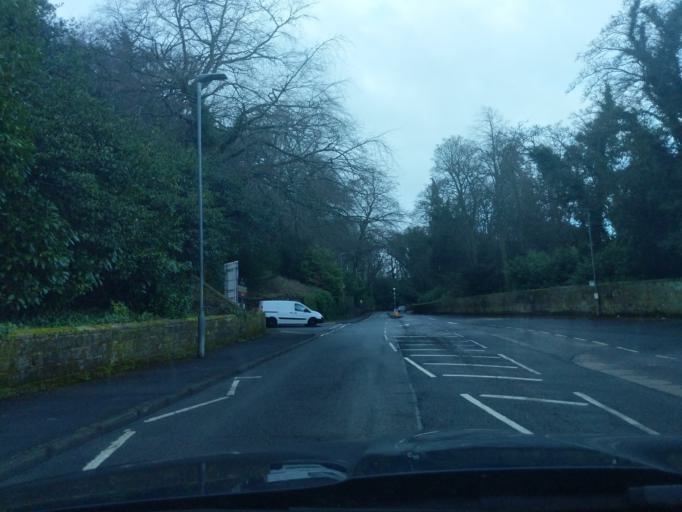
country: GB
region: England
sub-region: Northumberland
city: Alnwick
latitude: 55.4132
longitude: -1.6972
